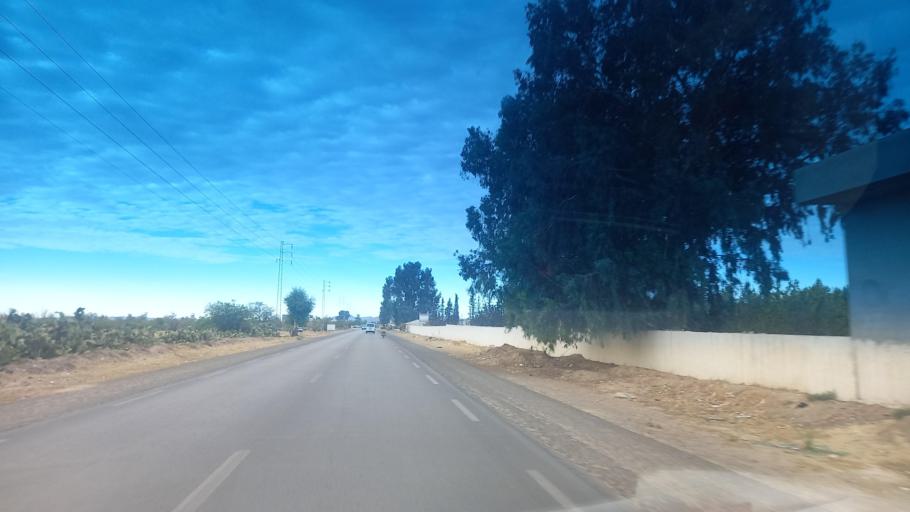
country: TN
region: Al Qasrayn
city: Kasserine
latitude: 35.2663
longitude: 9.0930
